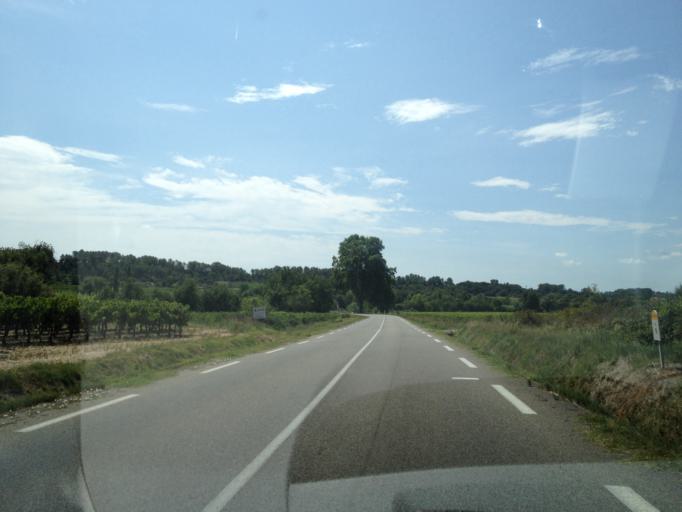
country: FR
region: Languedoc-Roussillon
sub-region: Departement du Gard
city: Villevieille
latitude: 43.8420
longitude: 4.0985
